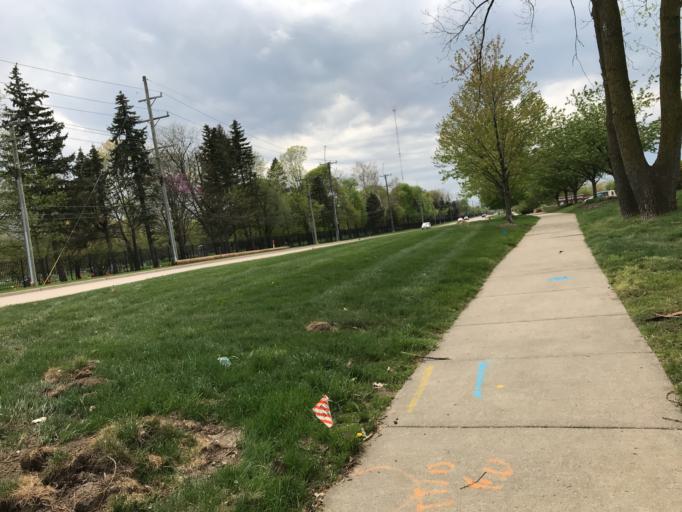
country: US
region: Michigan
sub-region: Oakland County
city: Bingham Farms
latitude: 42.4862
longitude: -83.2941
